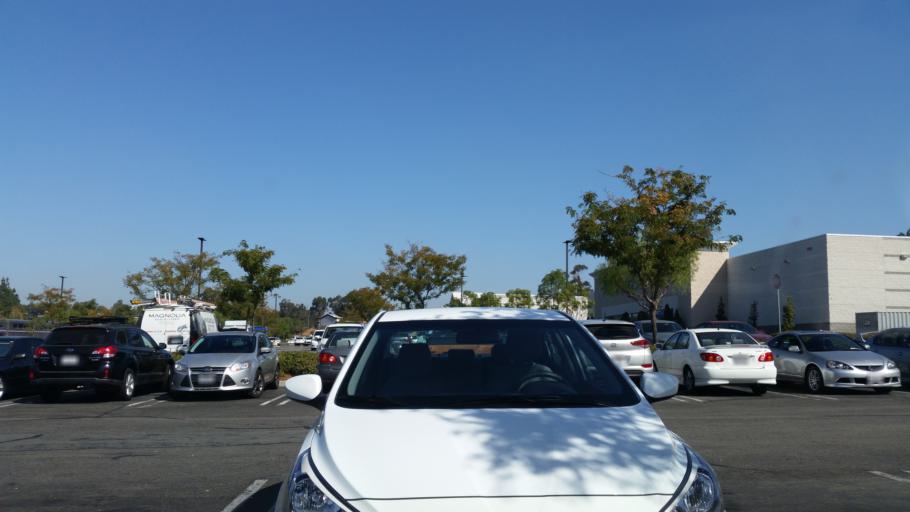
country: US
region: California
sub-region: Orange County
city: Mission Viejo
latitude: 33.5911
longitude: -117.6734
